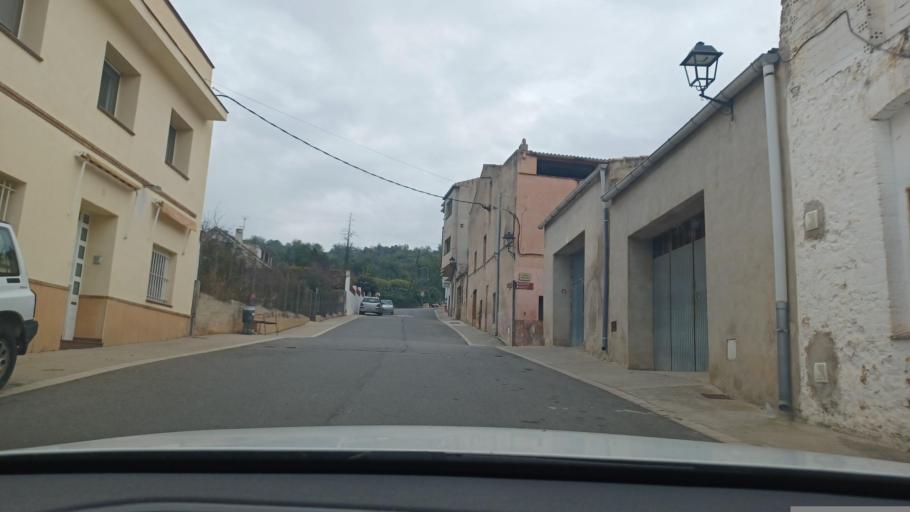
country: ES
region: Catalonia
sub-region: Provincia de Tarragona
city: Ulldecona
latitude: 40.6563
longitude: 0.4695
